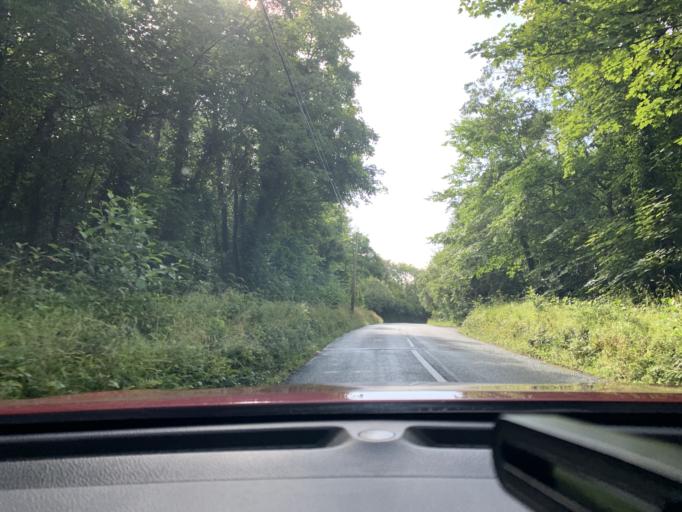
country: IE
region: Connaught
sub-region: Sligo
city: Strandhill
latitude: 54.3540
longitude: -8.5669
